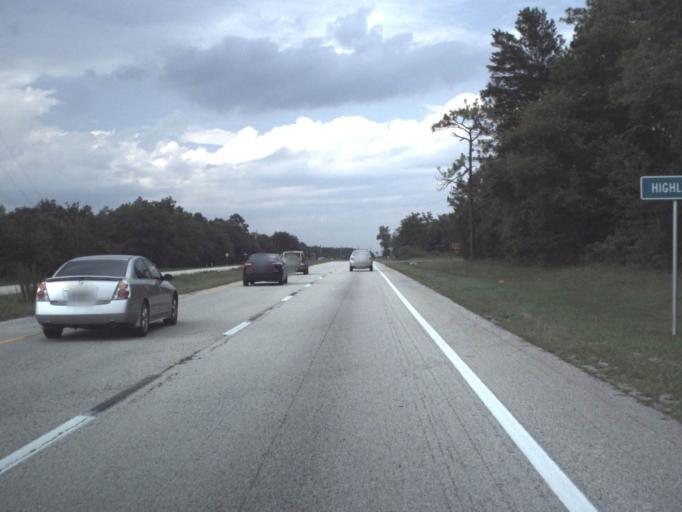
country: US
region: Florida
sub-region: Bradford County
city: Starke
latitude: 30.1068
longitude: -82.0508
